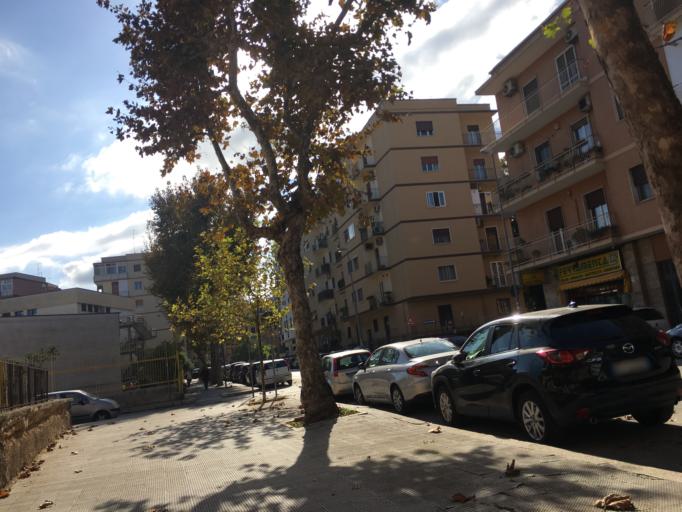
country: IT
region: Apulia
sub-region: Provincia di Bari
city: Bari
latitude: 41.1124
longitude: 16.8660
